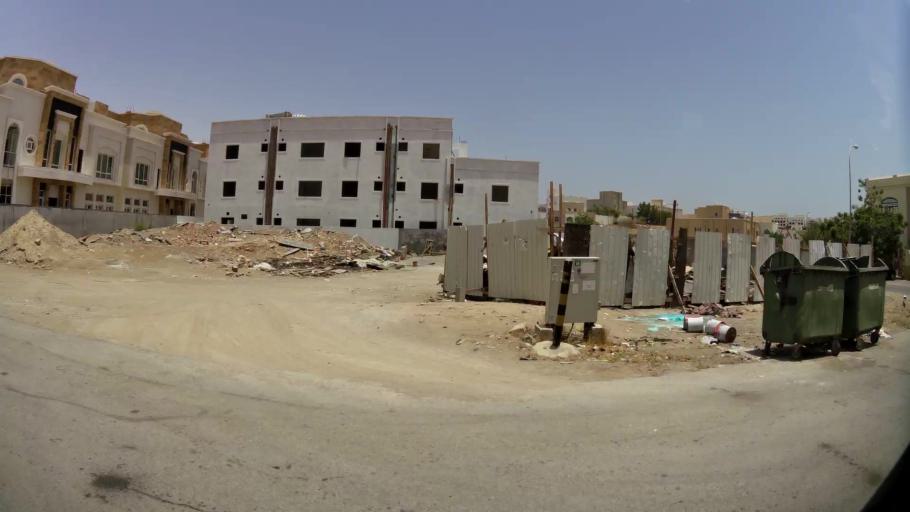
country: OM
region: Muhafazat Masqat
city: Bawshar
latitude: 23.5602
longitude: 58.4171
